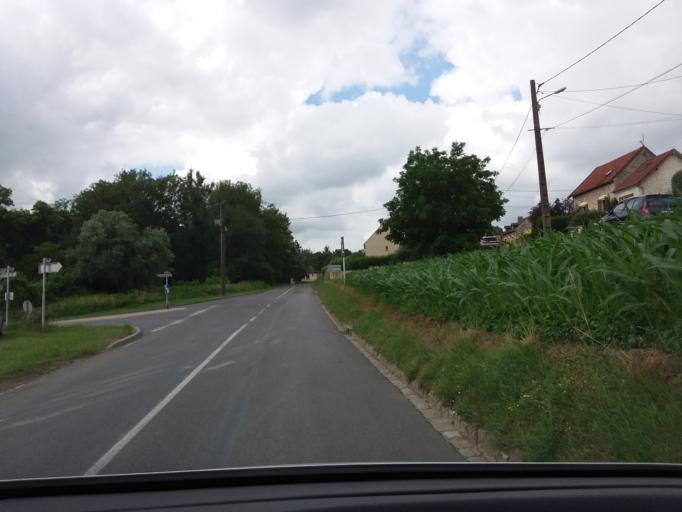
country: FR
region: Picardie
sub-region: Departement de l'Aisne
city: Vailly-sur-Aisne
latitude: 49.3999
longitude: 3.4743
